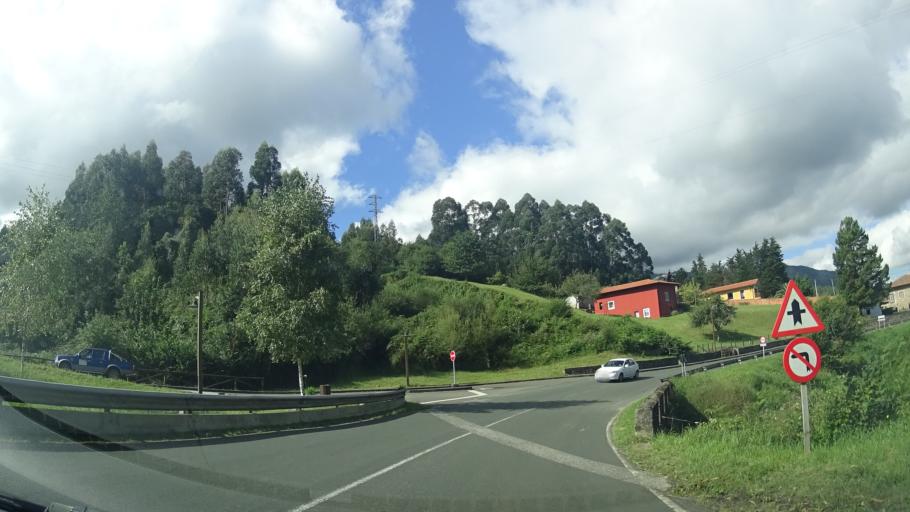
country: ES
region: Asturias
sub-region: Province of Asturias
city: Colunga
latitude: 43.4623
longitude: -5.2004
